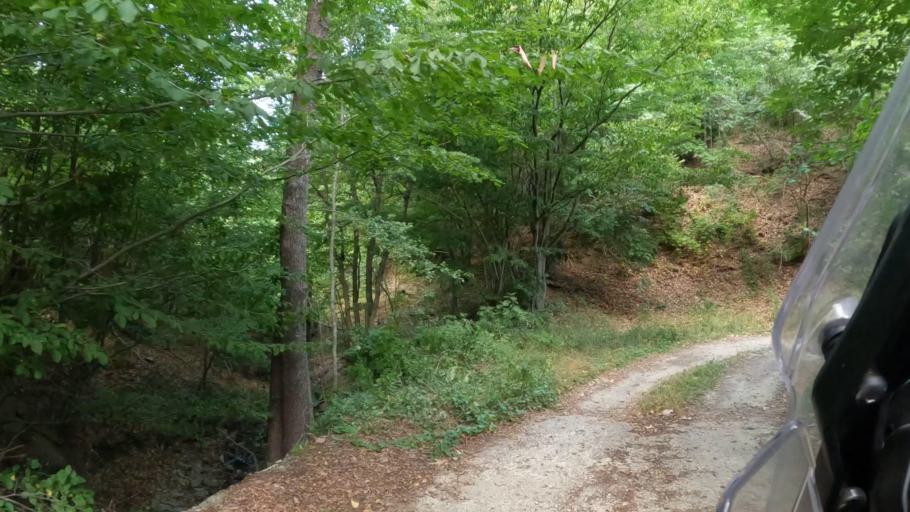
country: IT
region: Piedmont
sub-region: Provincia di Alessandria
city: Cassinelle-Concentrico
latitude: 44.5683
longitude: 8.5679
